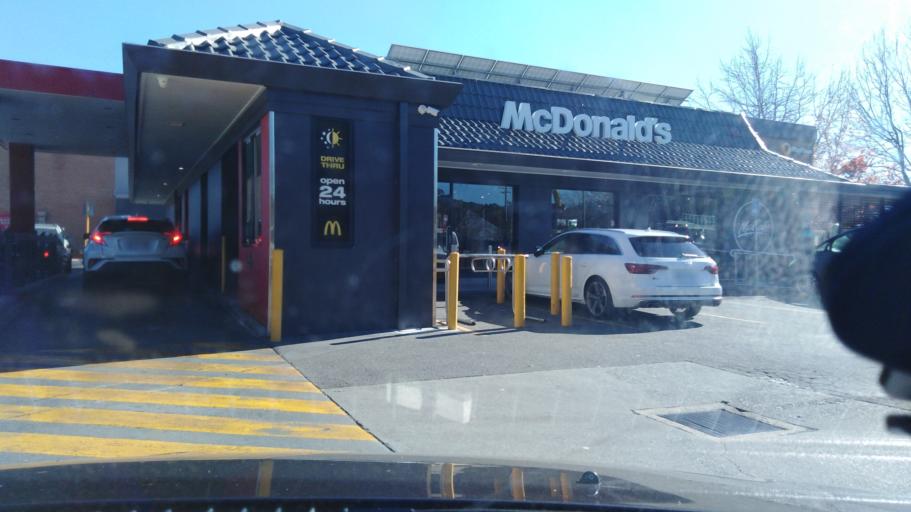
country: AU
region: Australian Capital Territory
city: Forrest
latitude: -35.3396
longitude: 149.0536
